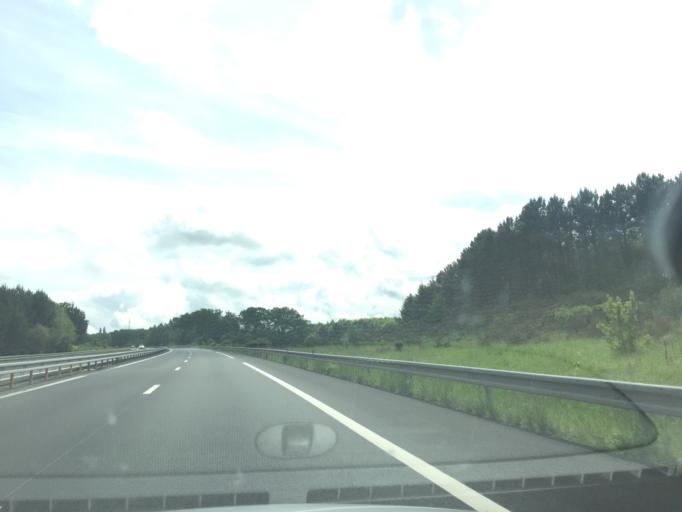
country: FR
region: Pays de la Loire
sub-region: Departement de la Sarthe
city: Ecommoy
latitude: 47.8569
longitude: 0.2974
